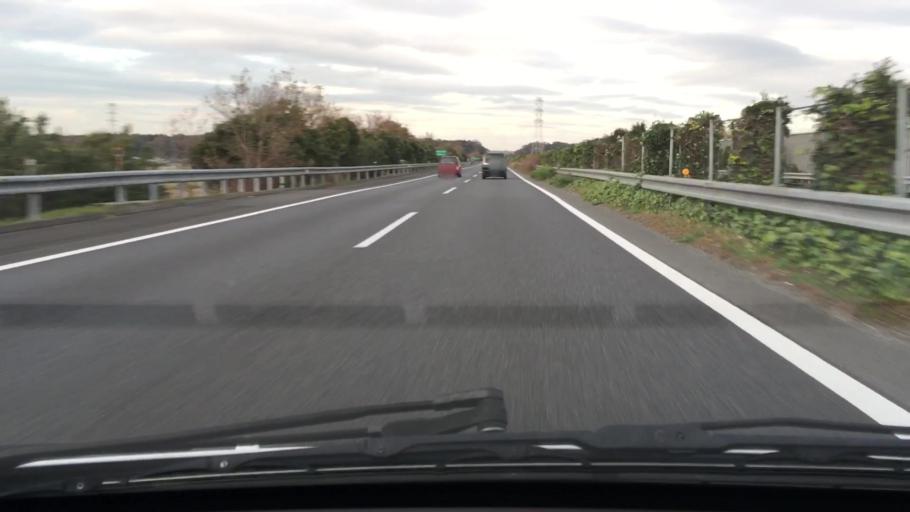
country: JP
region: Chiba
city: Kisarazu
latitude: 35.4049
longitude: 140.0080
